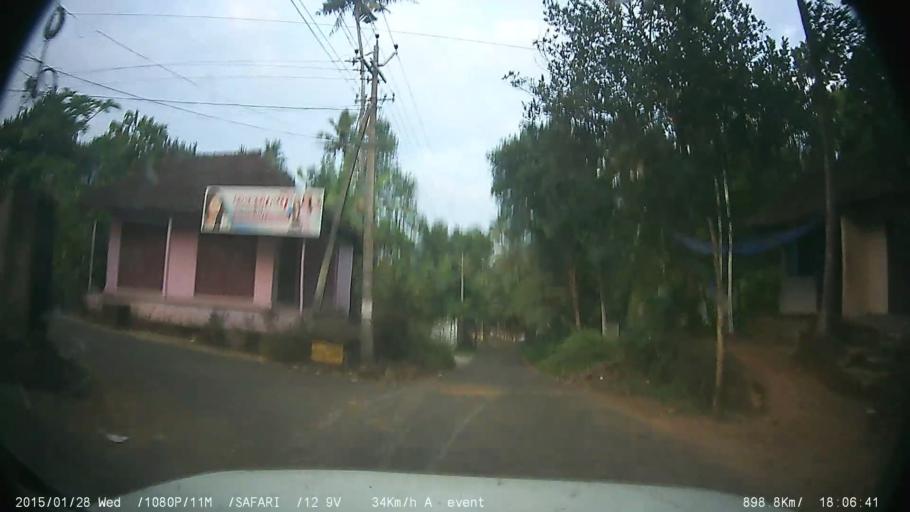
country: IN
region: Kerala
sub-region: Kottayam
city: Palackattumala
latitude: 9.7304
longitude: 76.5758
